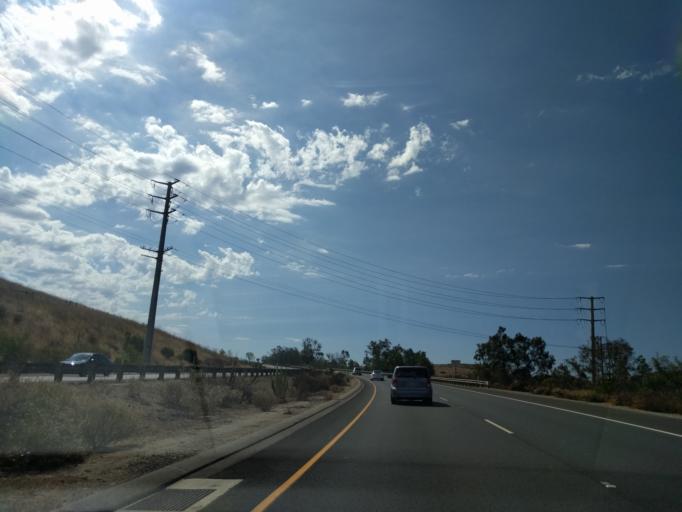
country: US
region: California
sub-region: Orange County
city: Laguna Woods
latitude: 33.6309
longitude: -117.7613
